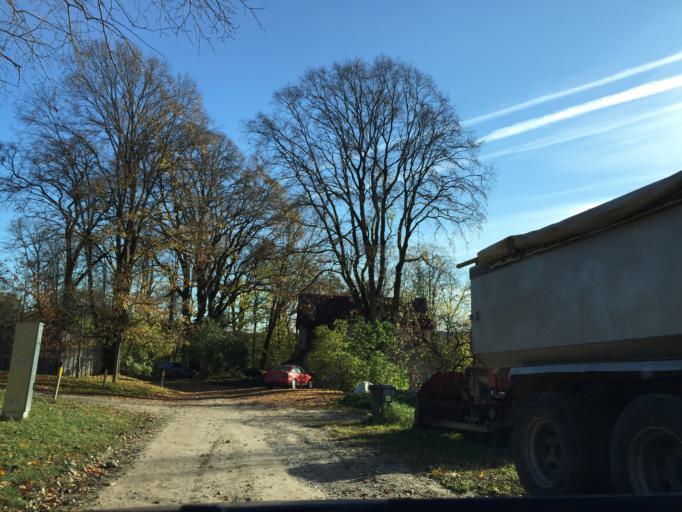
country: LV
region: Skriveri
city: Skriveri
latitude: 56.6154
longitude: 25.1579
